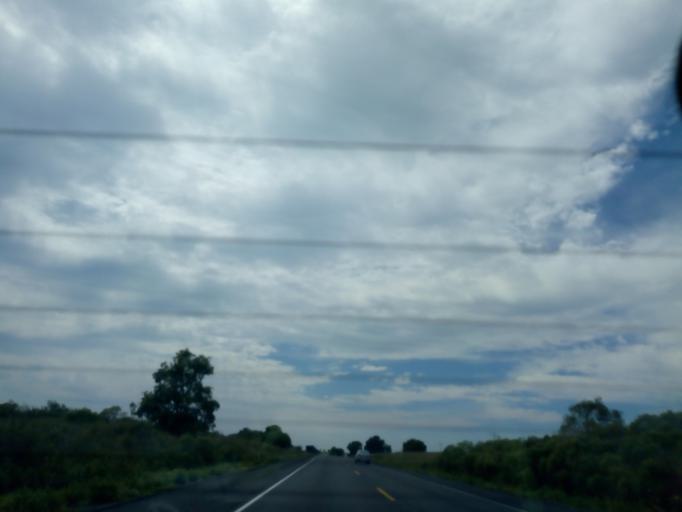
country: BR
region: Rio Grande do Sul
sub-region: Quarai
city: Quarai
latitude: -29.9694
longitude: -56.5618
